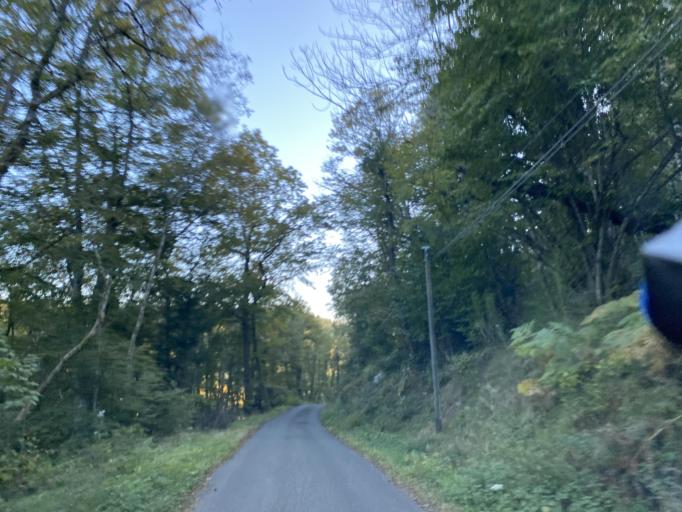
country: FR
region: Rhone-Alpes
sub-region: Departement de la Loire
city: Saint-Just-en-Chevalet
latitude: 45.9541
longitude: 3.8625
